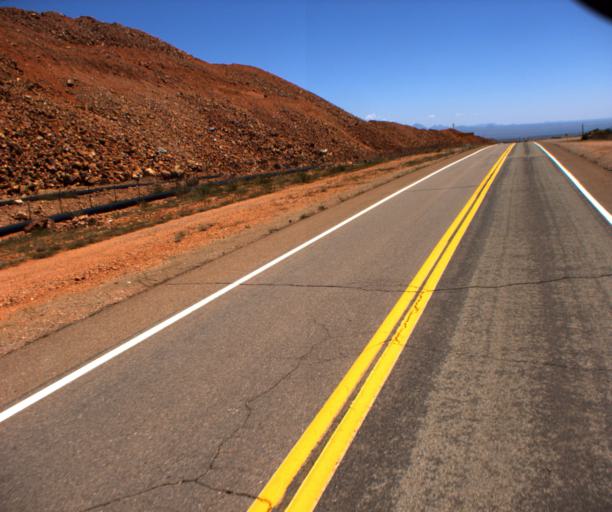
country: US
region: Arizona
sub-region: Greenlee County
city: Morenci
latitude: 33.0991
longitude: -109.3809
